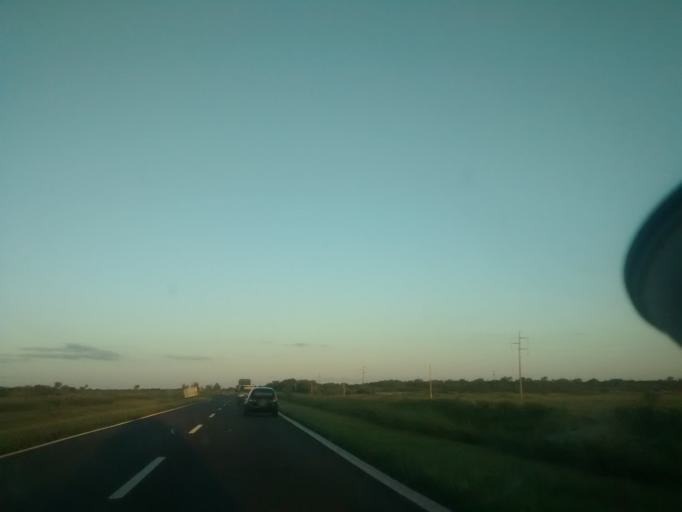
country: AR
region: Chaco
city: La Escondida
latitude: -27.1308
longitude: -59.4911
